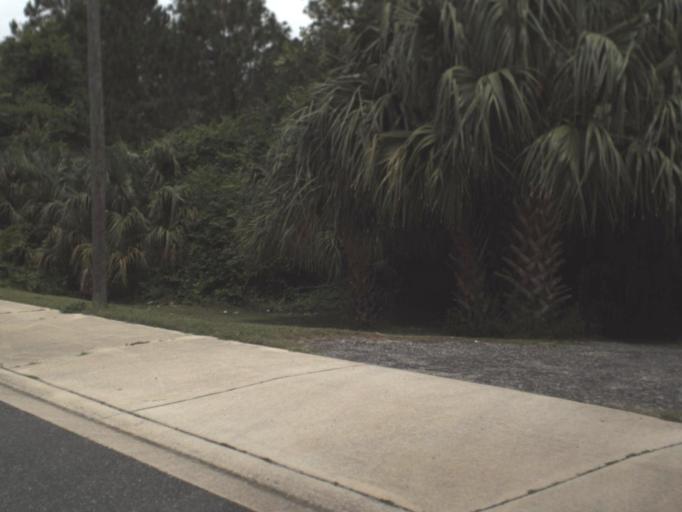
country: US
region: Florida
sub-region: Putnam County
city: Palatka
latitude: 29.6343
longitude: -81.7101
